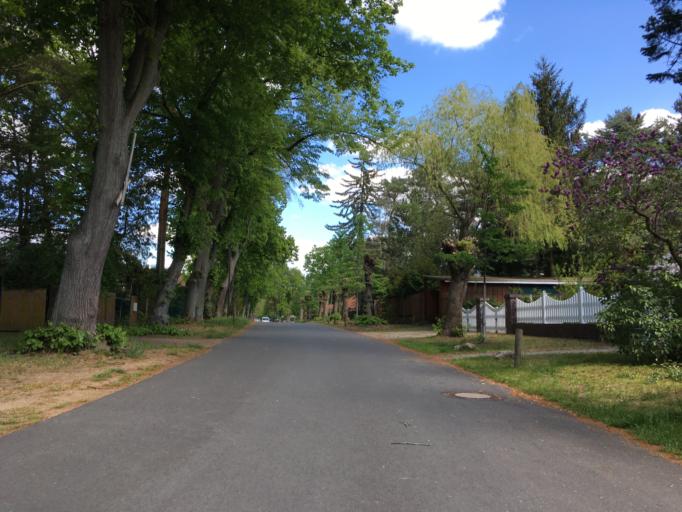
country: DE
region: Berlin
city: Blankenfelde
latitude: 52.6460
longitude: 13.3788
